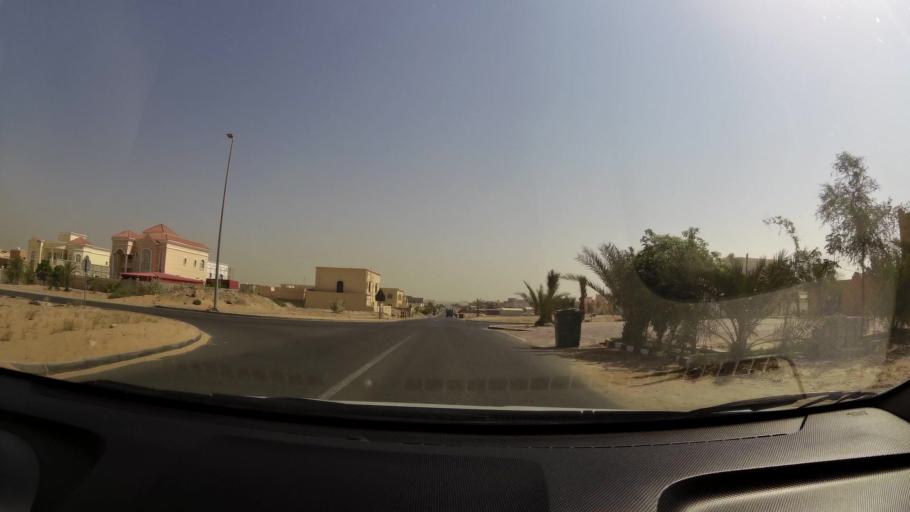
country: AE
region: Ajman
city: Ajman
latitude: 25.4083
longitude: 55.5405
